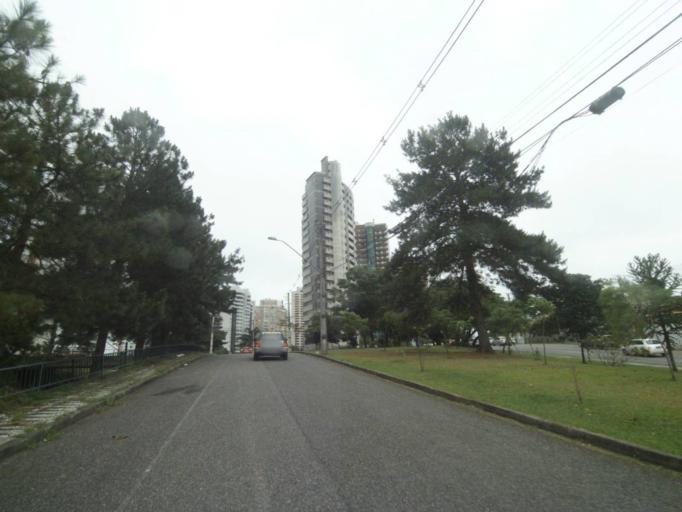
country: BR
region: Parana
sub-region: Curitiba
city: Curitiba
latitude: -25.4372
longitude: -49.3221
